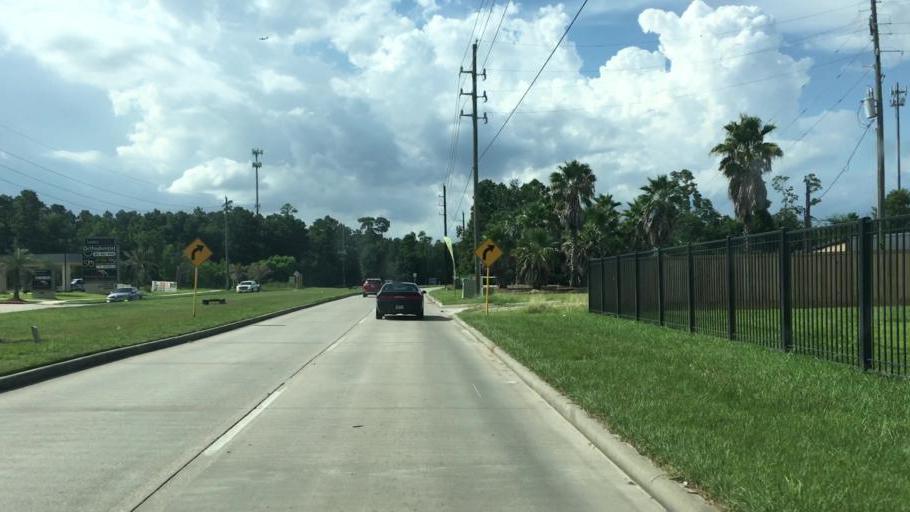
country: US
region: Texas
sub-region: Harris County
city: Atascocita
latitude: 29.9708
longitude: -95.1710
